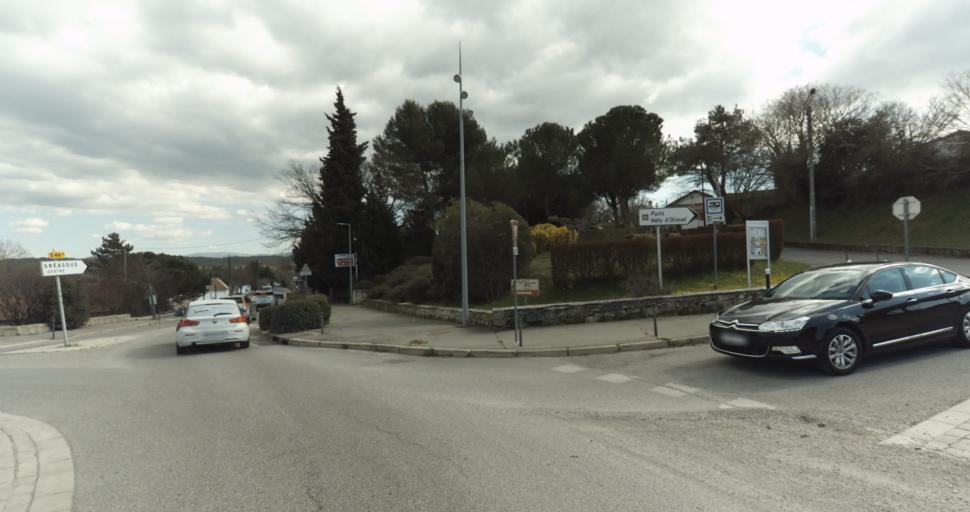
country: FR
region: Provence-Alpes-Cote d'Azur
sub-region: Departement des Bouches-du-Rhone
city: Greasque
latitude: 43.4347
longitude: 5.5385
